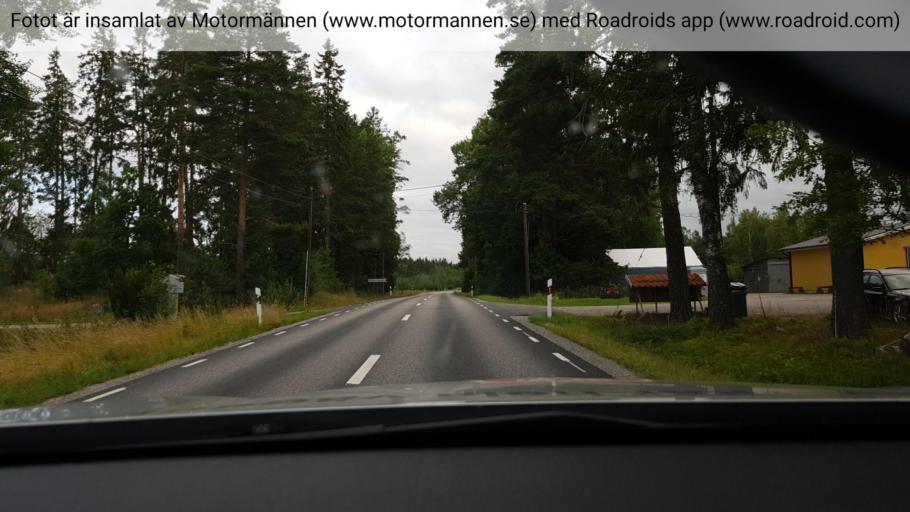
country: SE
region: Stockholm
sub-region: Norrtalje Kommun
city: Rimbo
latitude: 59.8239
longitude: 18.4403
